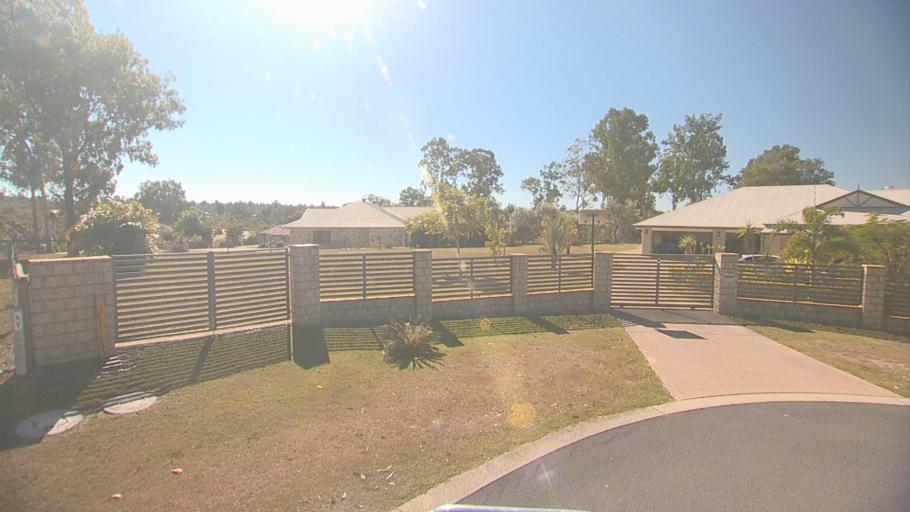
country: AU
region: Queensland
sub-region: Logan
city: North Maclean
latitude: -27.7539
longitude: 152.9614
